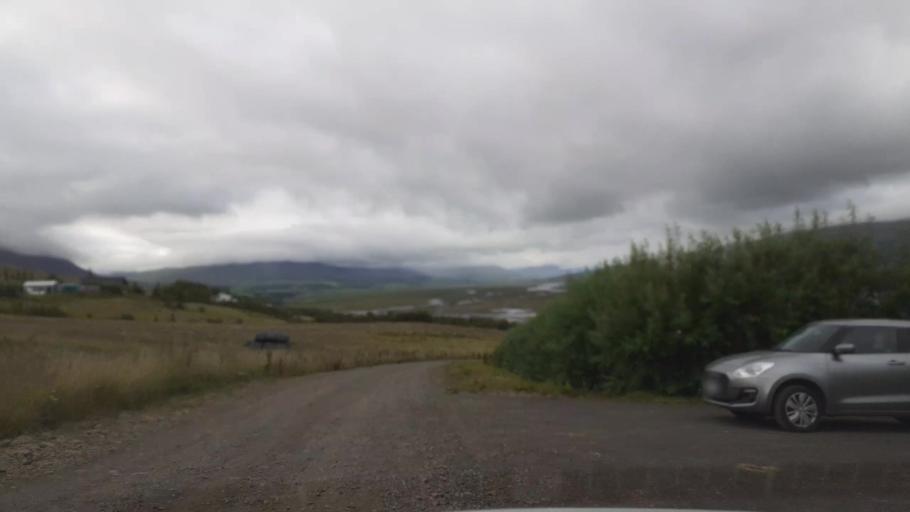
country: IS
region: Northeast
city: Akureyri
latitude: 65.6770
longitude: -18.0397
